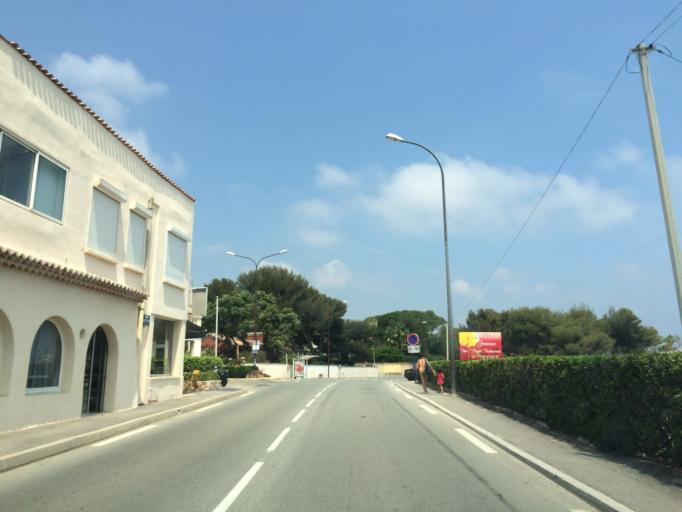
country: FR
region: Provence-Alpes-Cote d'Azur
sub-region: Departement du Var
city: Sainte-Maxime
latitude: 43.3249
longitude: 6.6648
